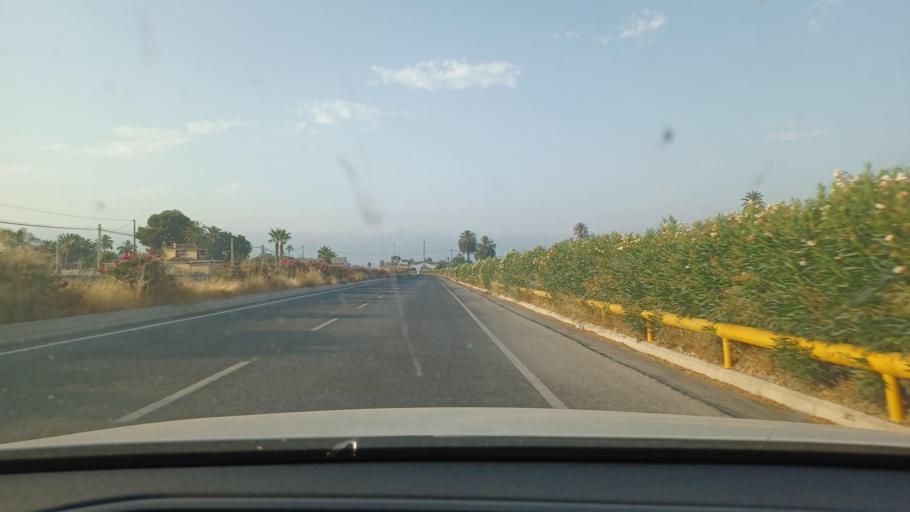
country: ES
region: Valencia
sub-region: Provincia de Alicante
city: Elche
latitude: 38.2275
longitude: -0.6994
